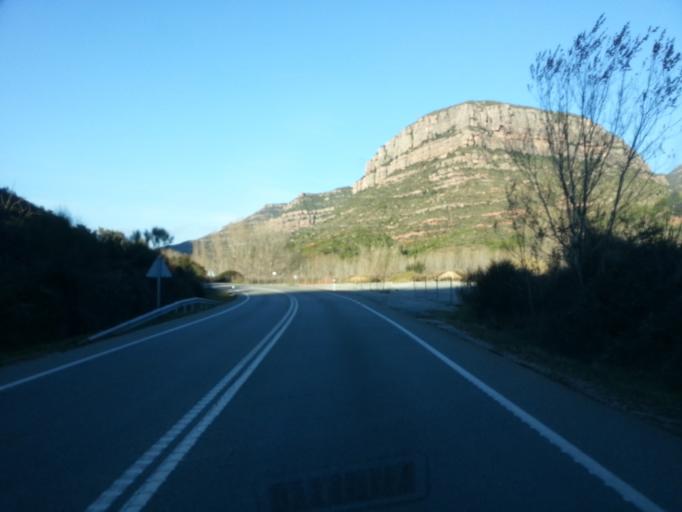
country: ES
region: Catalonia
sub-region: Provincia de Barcelona
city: Collbato
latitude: 41.5713
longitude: 1.8635
